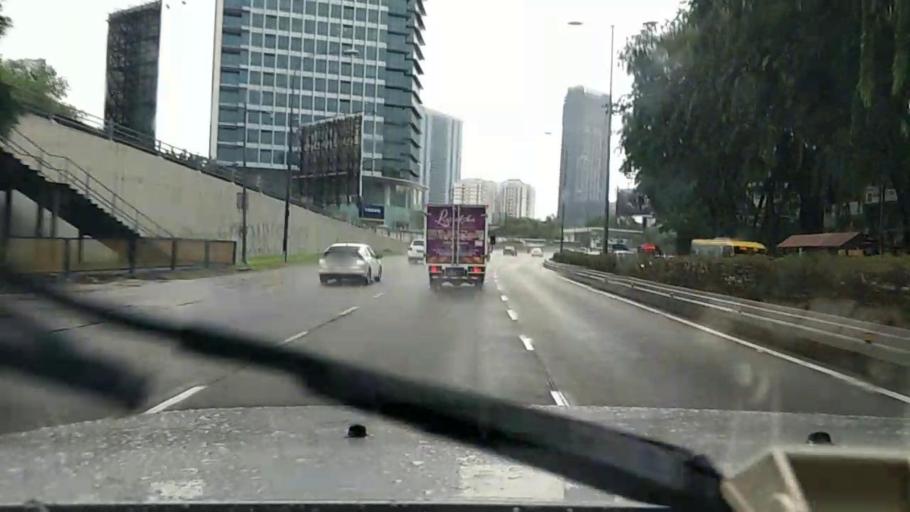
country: MY
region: Kuala Lumpur
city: Kuala Lumpur
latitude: 3.1196
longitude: 101.6794
